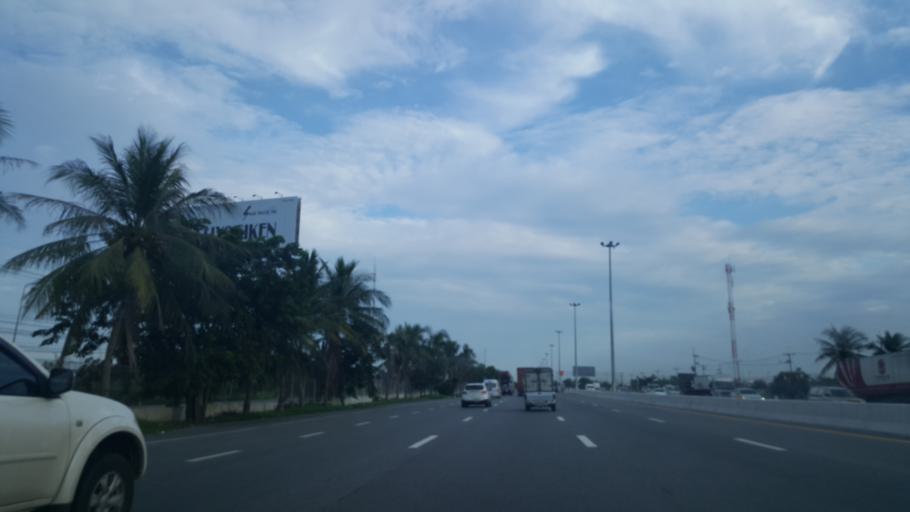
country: TH
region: Chachoengsao
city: Bang Pakong
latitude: 13.5360
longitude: 101.0117
